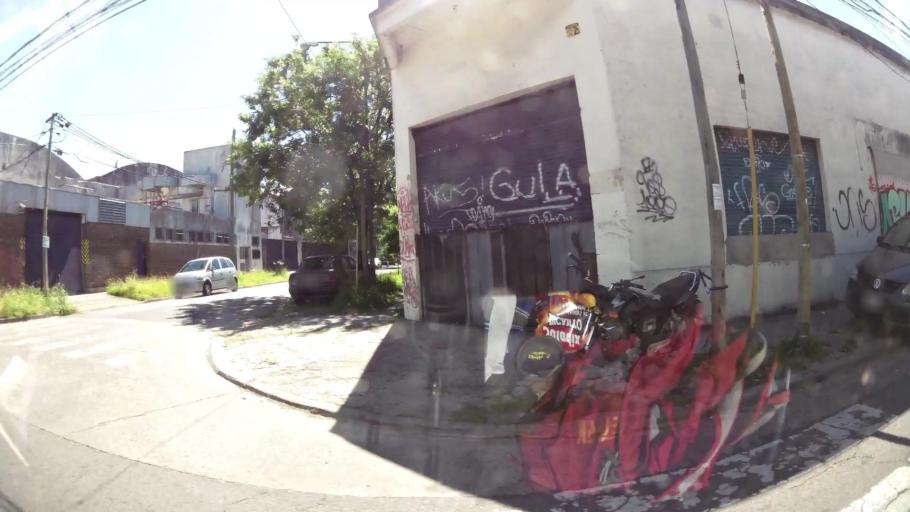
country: AR
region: Buenos Aires
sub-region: Partido de General San Martin
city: General San Martin
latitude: -34.5390
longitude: -58.5391
